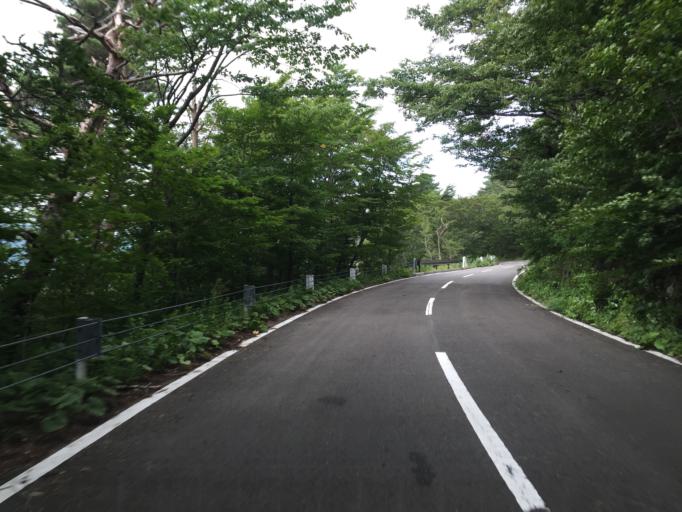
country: JP
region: Fukushima
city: Nihommatsu
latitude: 37.6594
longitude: 140.3216
